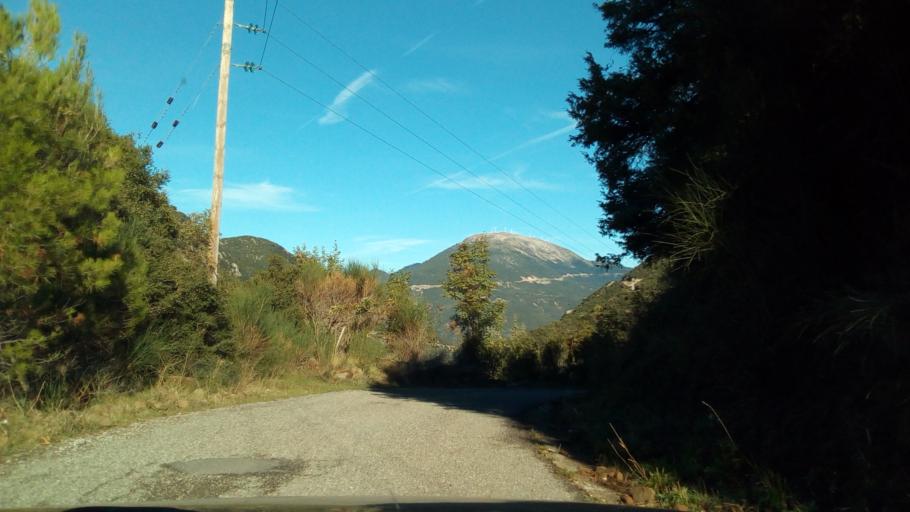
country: GR
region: West Greece
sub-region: Nomos Aitolias kai Akarnanias
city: Nafpaktos
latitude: 38.5597
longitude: 21.8528
